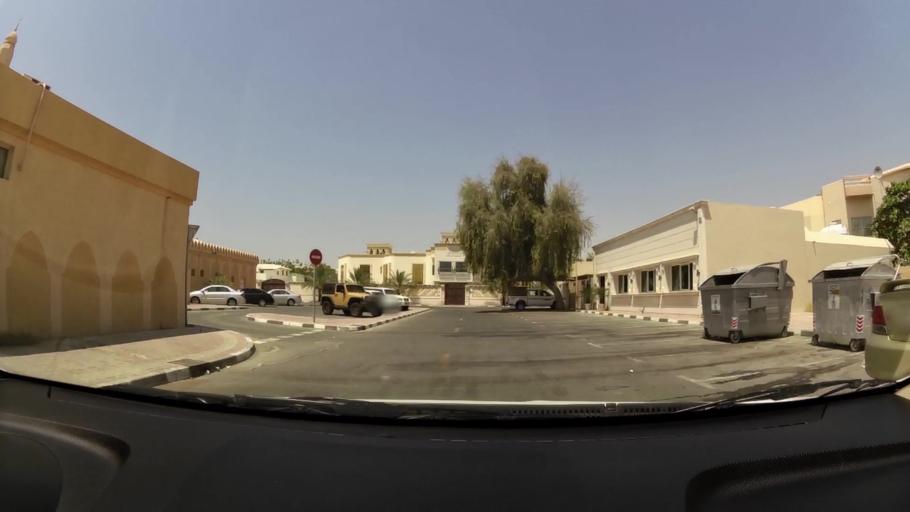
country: AE
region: Ash Shariqah
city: Sharjah
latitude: 25.2922
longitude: 55.3443
